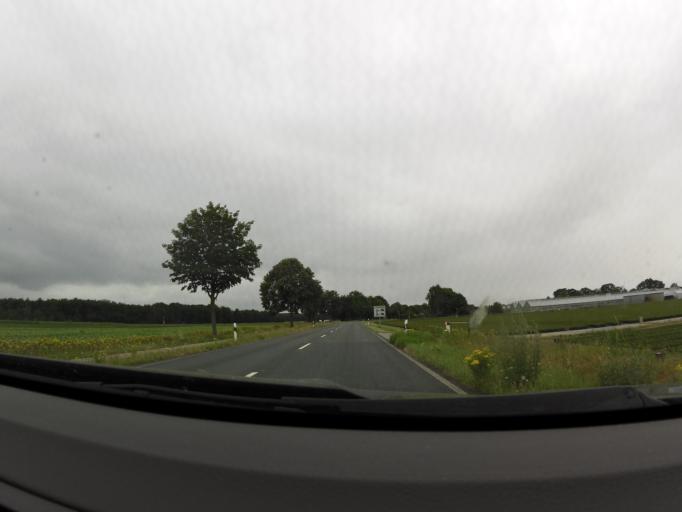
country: DE
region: North Rhine-Westphalia
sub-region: Regierungsbezirk Dusseldorf
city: Kevelaer
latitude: 51.5515
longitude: 6.2412
